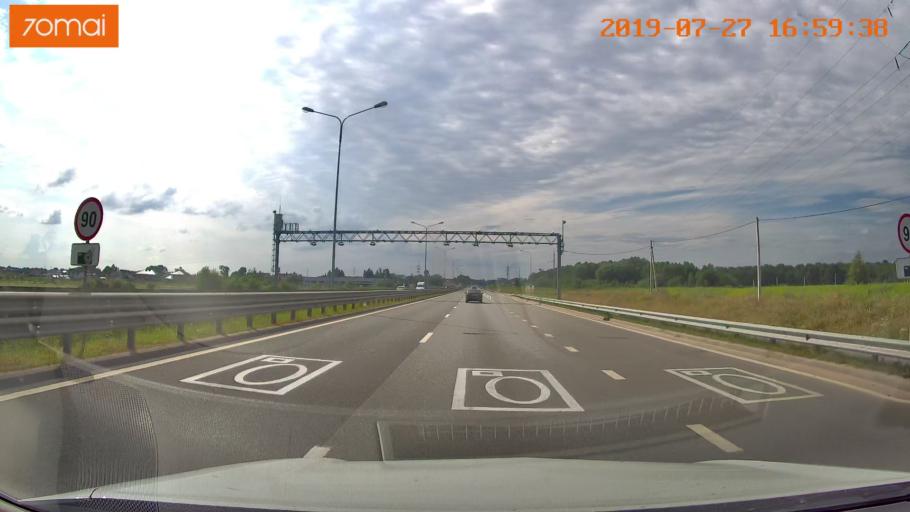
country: RU
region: Kaliningrad
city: Bol'shoe Isakovo
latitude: 54.7049
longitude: 20.6448
